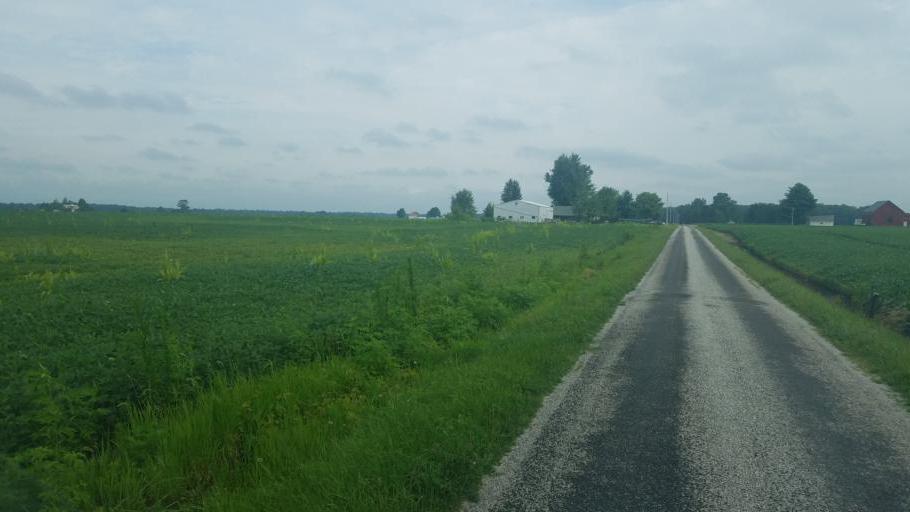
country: US
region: Ohio
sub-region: Morrow County
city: Cardington
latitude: 40.5071
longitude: -82.9816
